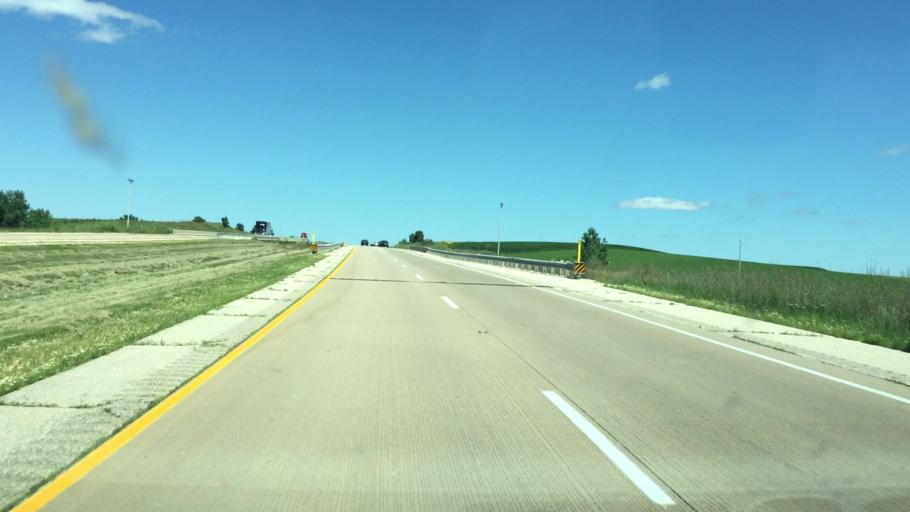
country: US
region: Wisconsin
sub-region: Grant County
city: Platteville
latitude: 42.7377
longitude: -90.4089
